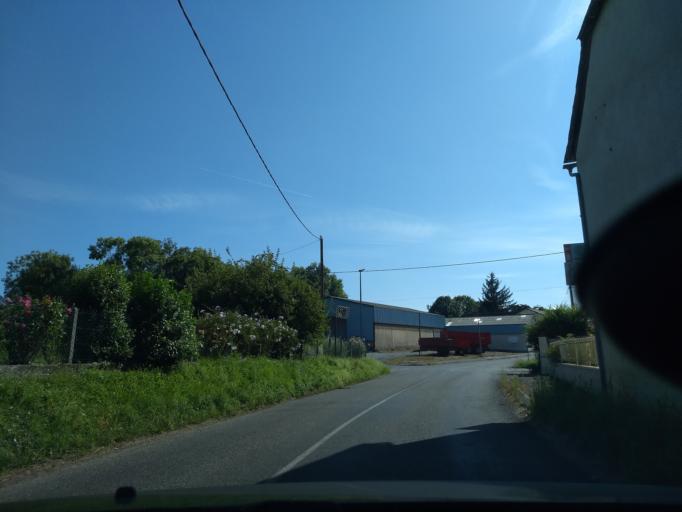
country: FR
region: Aquitaine
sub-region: Departement des Pyrenees-Atlantiques
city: Soumoulou
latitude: 43.2897
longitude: -0.1598
